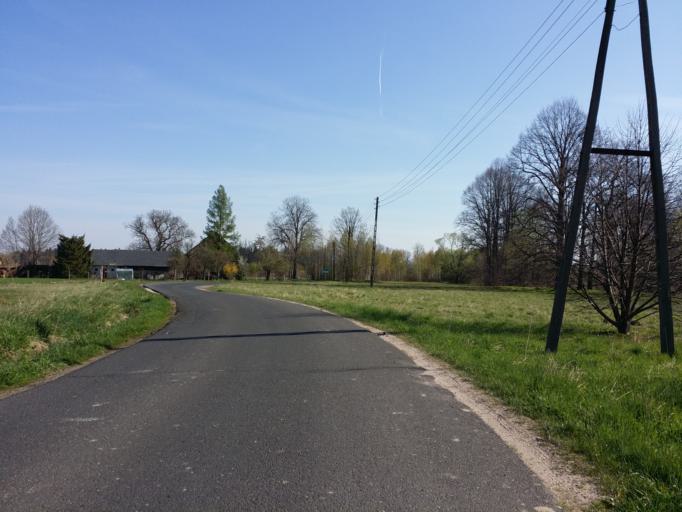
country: PL
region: Lower Silesian Voivodeship
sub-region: Powiat lwowecki
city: Mirsk
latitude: 50.9528
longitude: 15.4276
